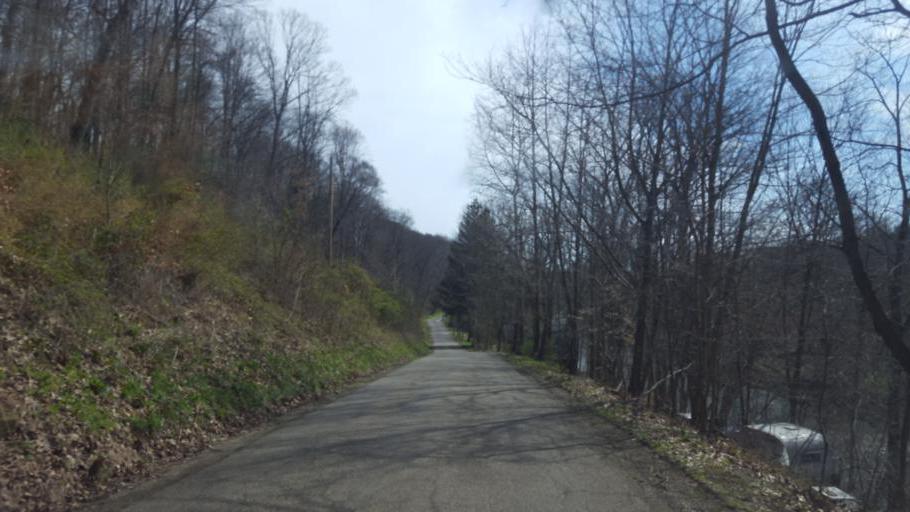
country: US
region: Ohio
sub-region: Knox County
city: Gambier
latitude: 40.3806
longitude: -82.4290
